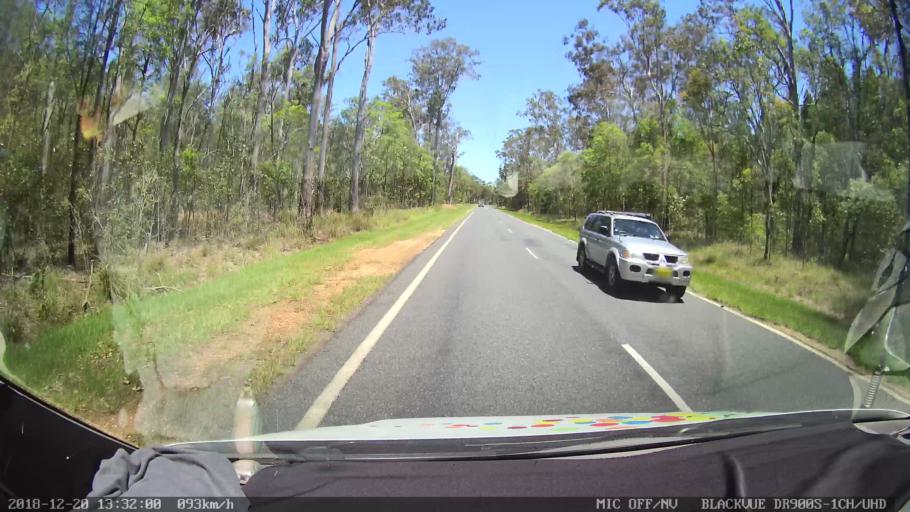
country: AU
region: New South Wales
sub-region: Clarence Valley
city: Gordon
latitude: -29.2260
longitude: 152.9882
